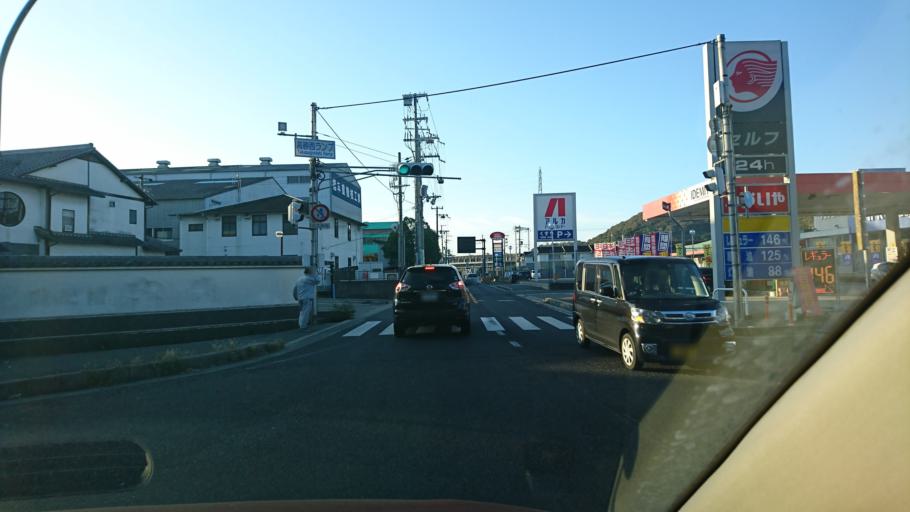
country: JP
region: Hyogo
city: Shirahamacho-usazakiminami
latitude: 34.7888
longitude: 134.7714
